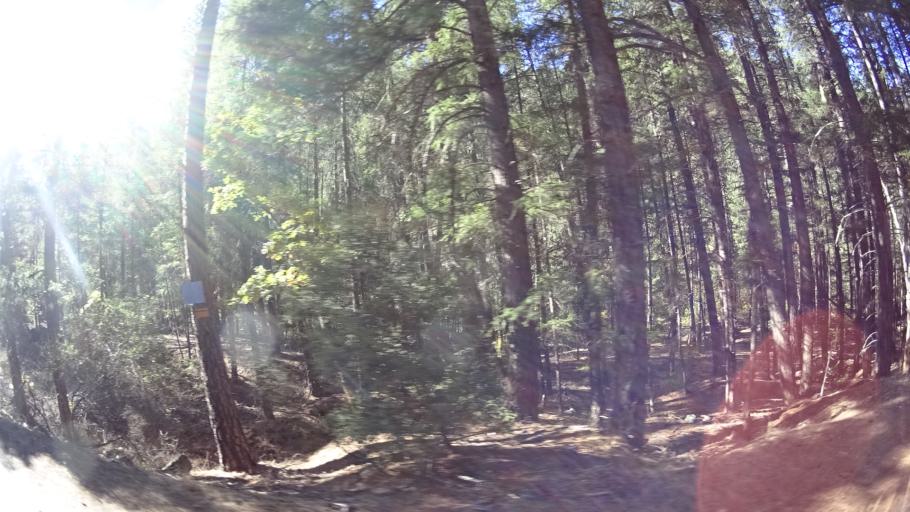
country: US
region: California
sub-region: Trinity County
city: Weaverville
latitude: 41.1451
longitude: -123.1046
